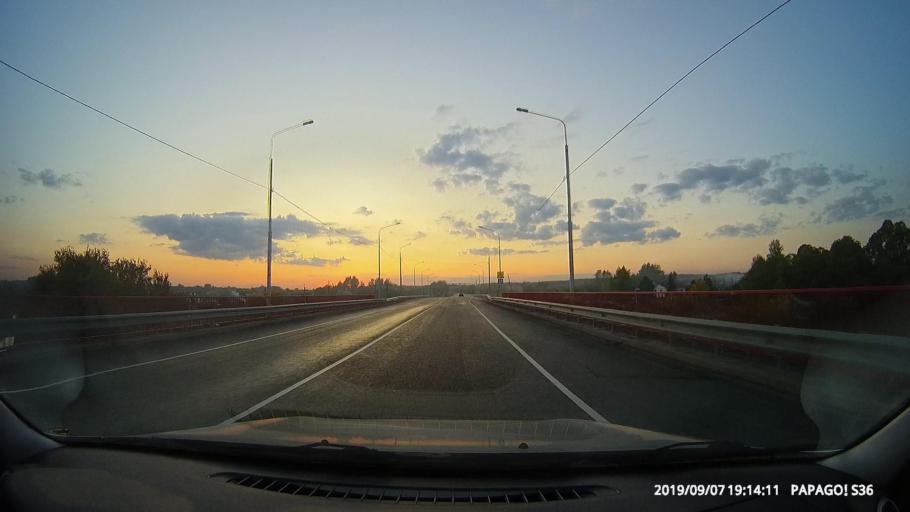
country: RU
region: Samara
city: Chapayevsk
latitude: 52.9972
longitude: 49.7754
